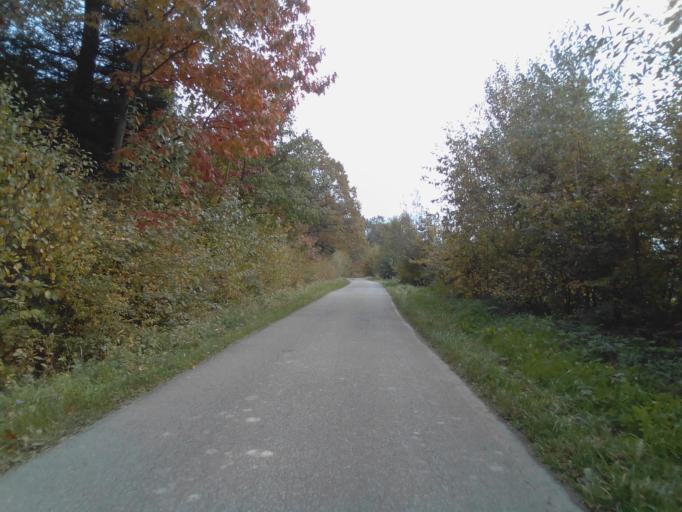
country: PL
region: Subcarpathian Voivodeship
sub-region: Powiat rzeszowski
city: Straszydle
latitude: 49.8634
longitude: 21.9685
